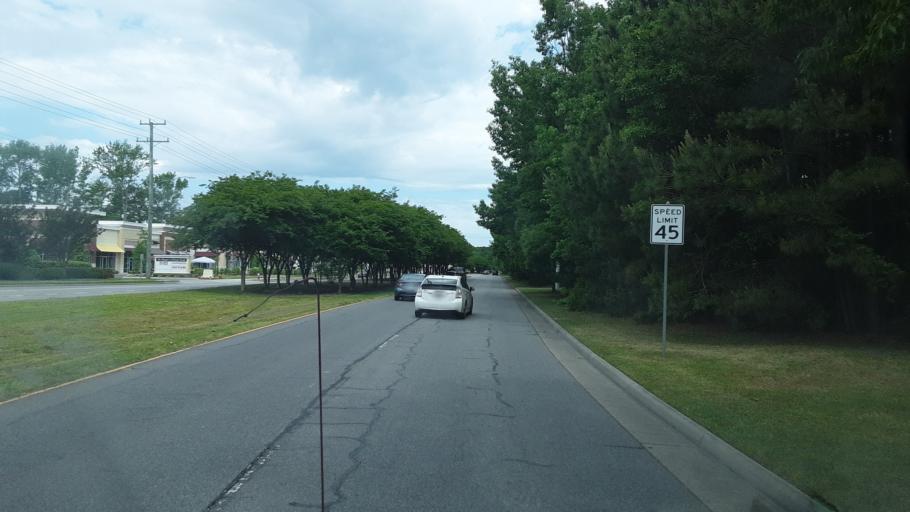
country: US
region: Virginia
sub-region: City of Virginia Beach
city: Virginia Beach
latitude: 36.7949
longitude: -75.9989
